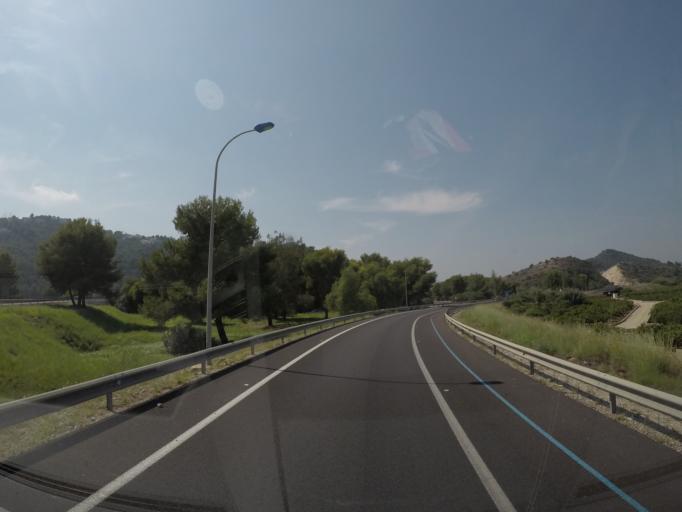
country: ES
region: Valencia
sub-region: Provincia de Valencia
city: L'Alqueria de la Comtessa
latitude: 38.9246
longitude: -0.1391
